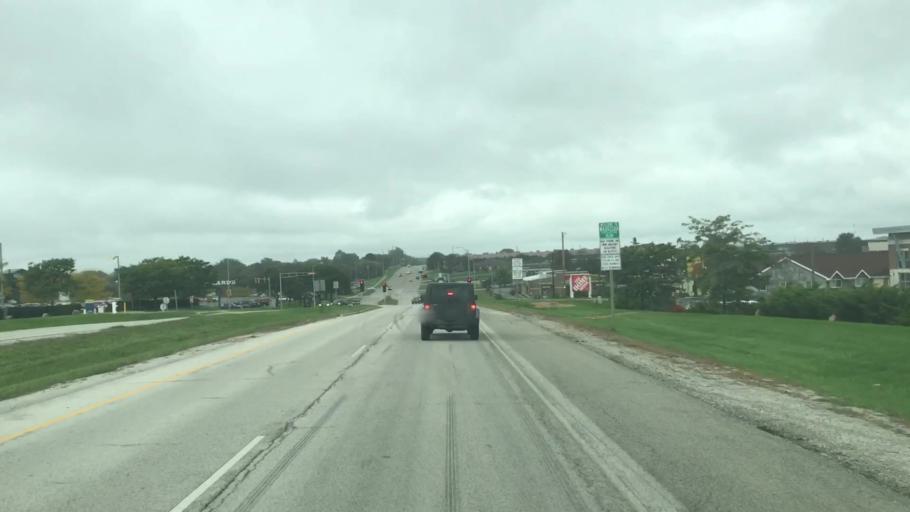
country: US
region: Wisconsin
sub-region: Waukesha County
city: Waukesha
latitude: 43.0365
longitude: -88.1771
